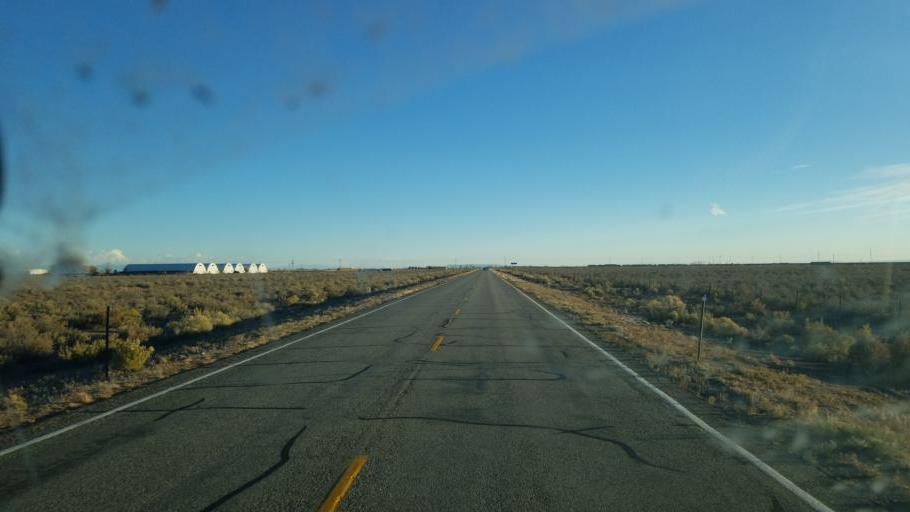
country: US
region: Colorado
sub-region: Saguache County
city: Center
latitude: 37.7117
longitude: -105.8768
